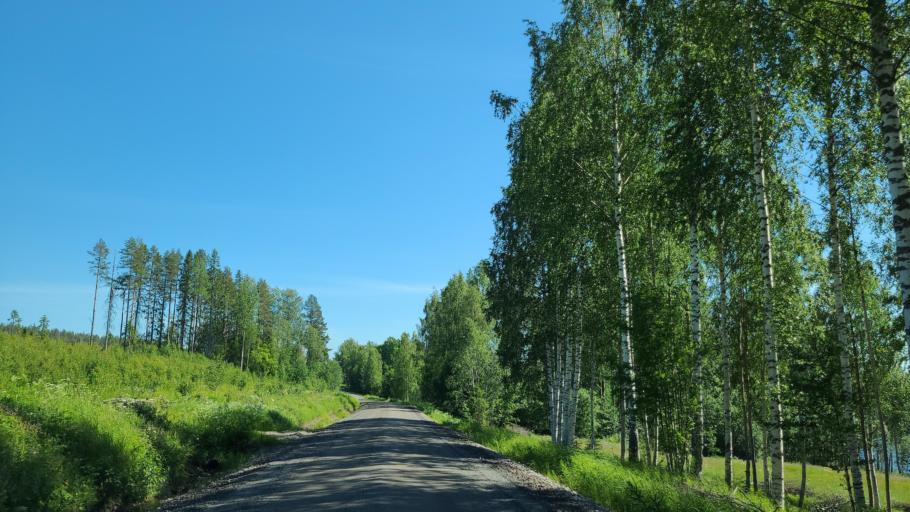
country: SE
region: Vaesterbotten
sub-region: Bjurholms Kommun
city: Bjurholm
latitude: 63.6700
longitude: 19.0648
